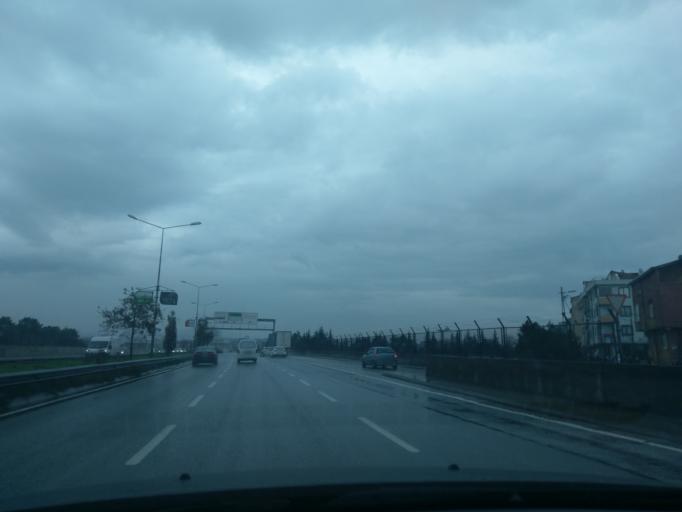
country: TR
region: Istanbul
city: Samandira
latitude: 41.0142
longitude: 29.1997
